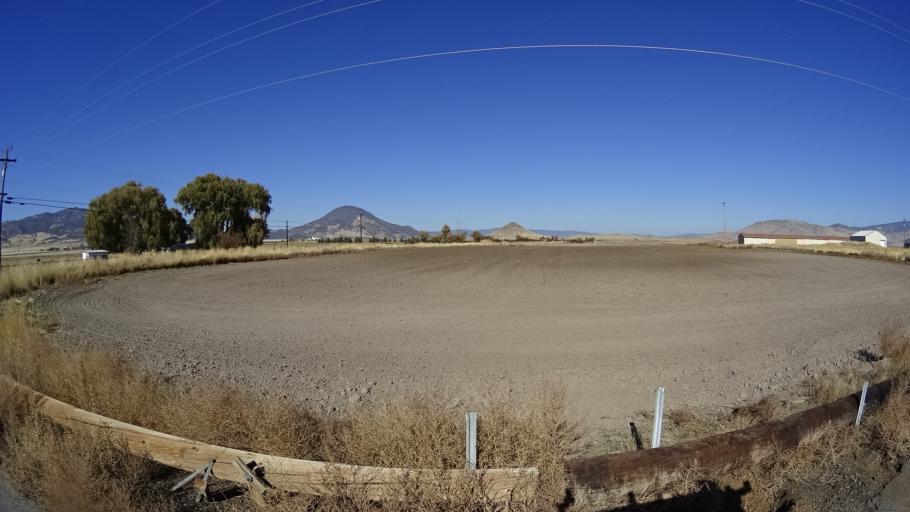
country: US
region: California
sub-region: Siskiyou County
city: Montague
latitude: 41.7810
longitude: -122.4731
